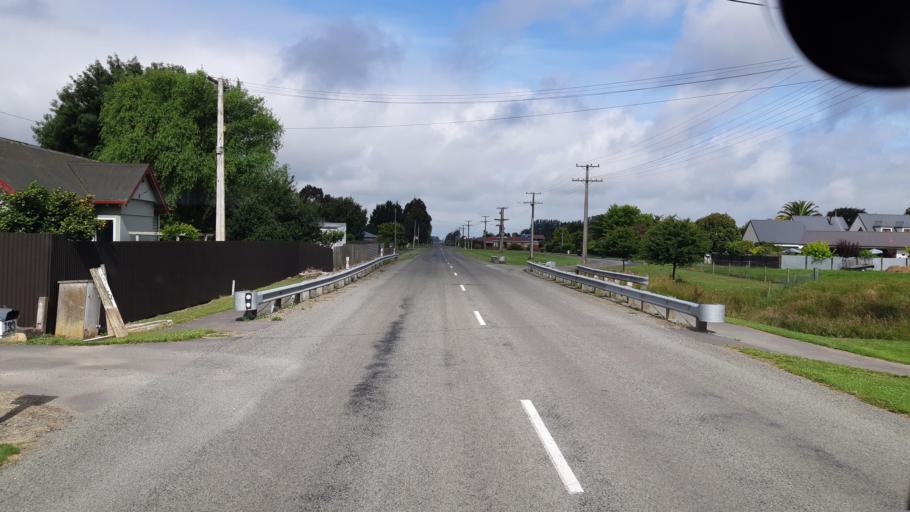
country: NZ
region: Canterbury
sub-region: Timaru District
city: Timaru
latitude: -44.2411
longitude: 171.2976
